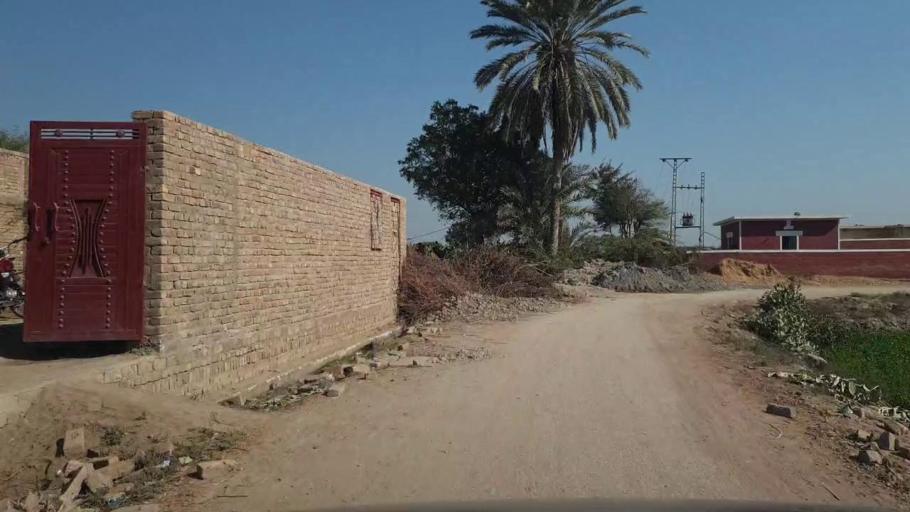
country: PK
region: Sindh
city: Shahpur Chakar
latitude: 26.1496
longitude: 68.6499
